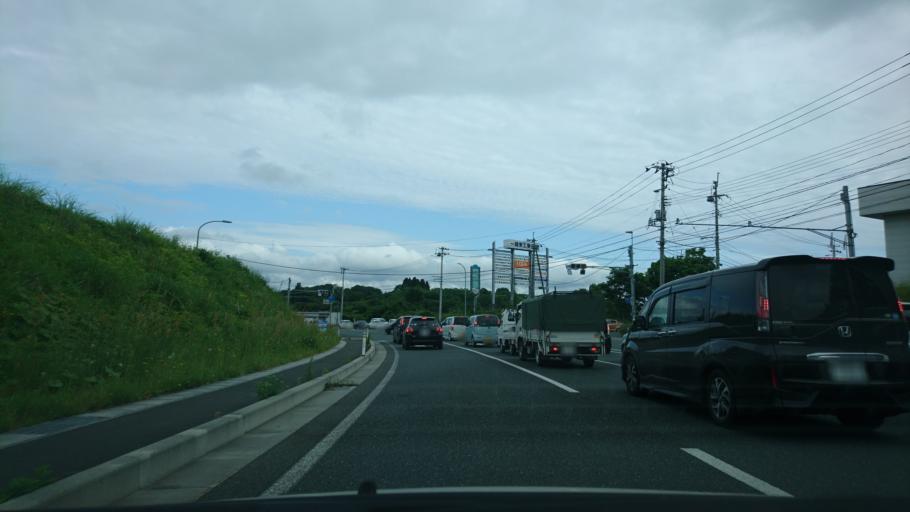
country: JP
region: Iwate
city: Ichinoseki
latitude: 38.9113
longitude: 141.1599
